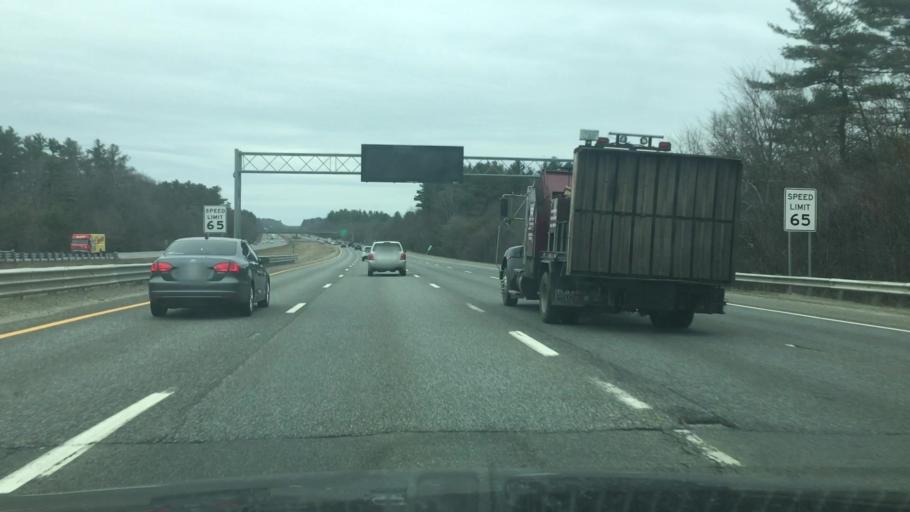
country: US
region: Massachusetts
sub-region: Essex County
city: Topsfield
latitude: 42.6348
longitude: -70.9770
